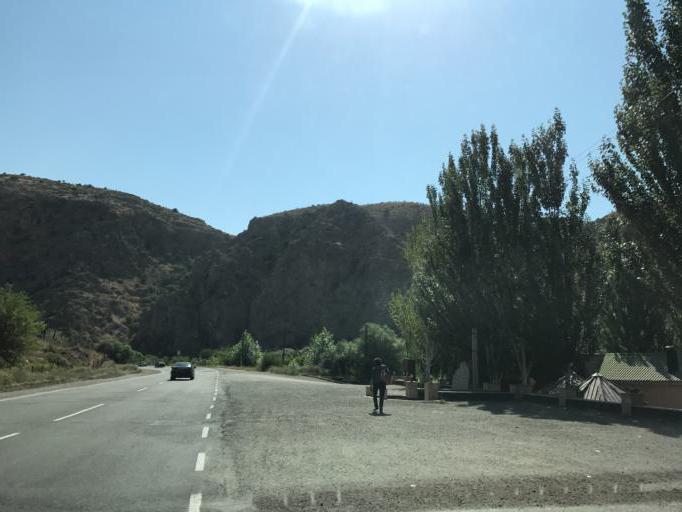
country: AM
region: Vayots' Dzori Marz
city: Areni
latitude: 39.7292
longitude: 45.2188
